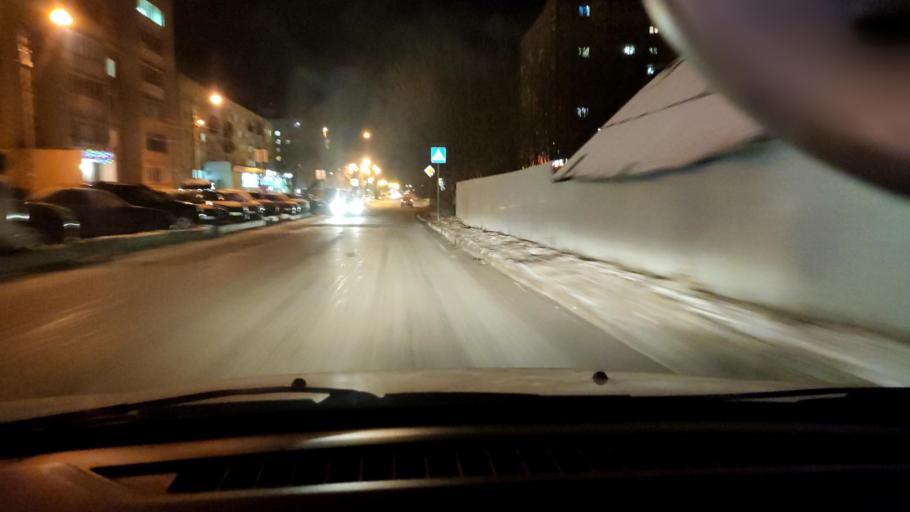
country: RU
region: Perm
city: Overyata
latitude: 58.0267
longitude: 55.8425
